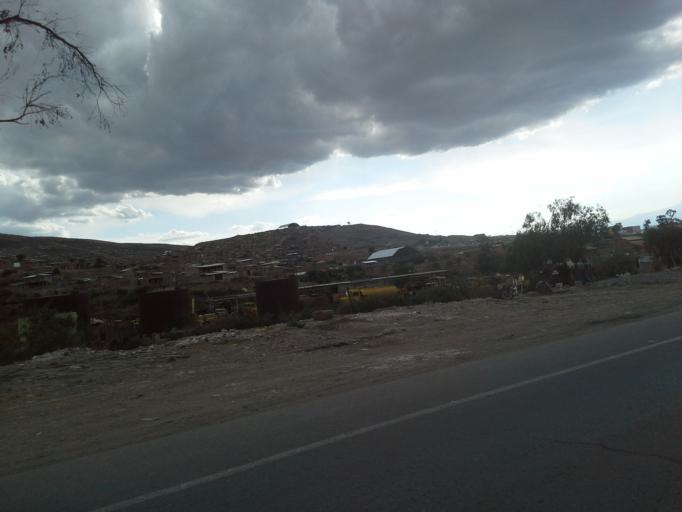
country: BO
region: Cochabamba
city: Cochabamba
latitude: -17.4659
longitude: -66.1189
